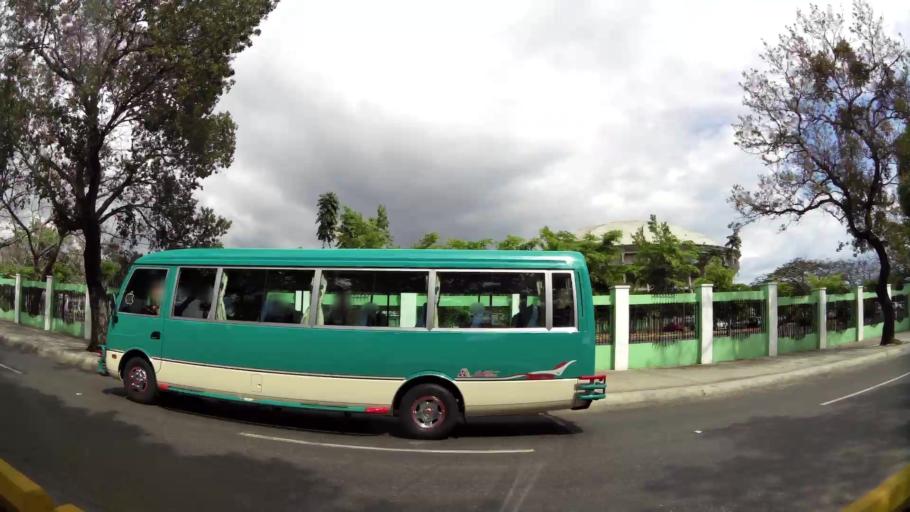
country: DO
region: Nacional
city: La Agustina
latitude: 18.4887
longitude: -69.9296
